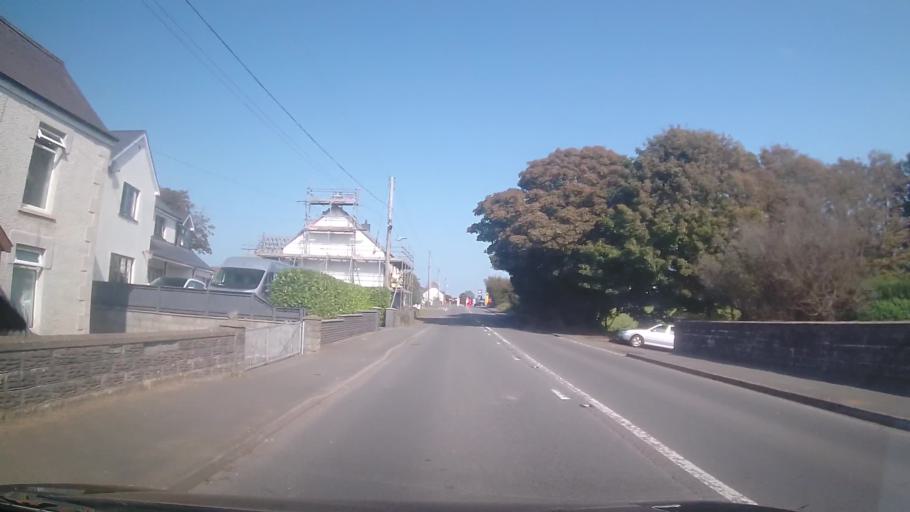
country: GB
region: Wales
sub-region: County of Ceredigion
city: Cardigan
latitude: 52.1001
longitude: -4.6141
